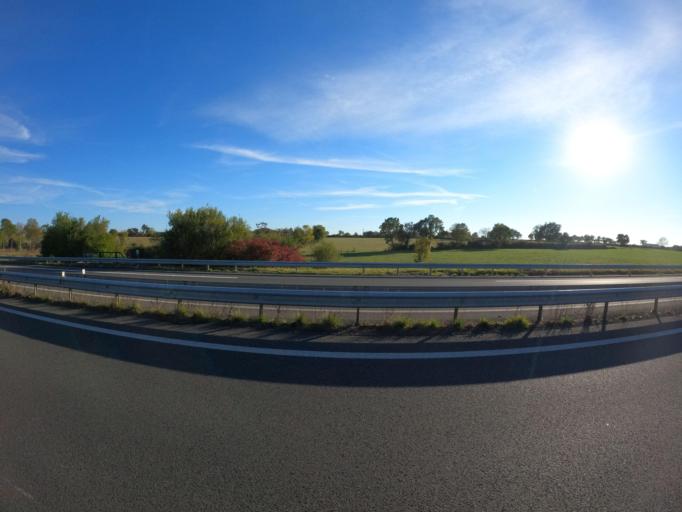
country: FR
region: Pays de la Loire
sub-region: Departement de Maine-et-Loire
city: Chemille-Melay
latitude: 47.2469
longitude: -0.6902
